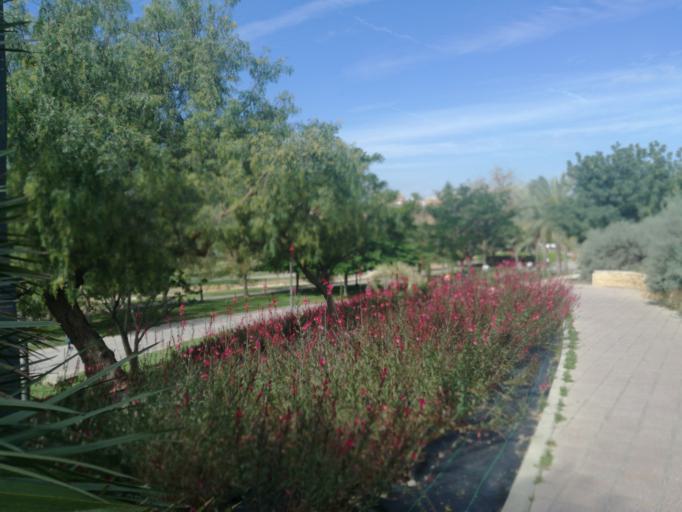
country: ES
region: Valencia
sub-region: Provincia de Valencia
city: Valencia
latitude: 39.4597
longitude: -0.3544
